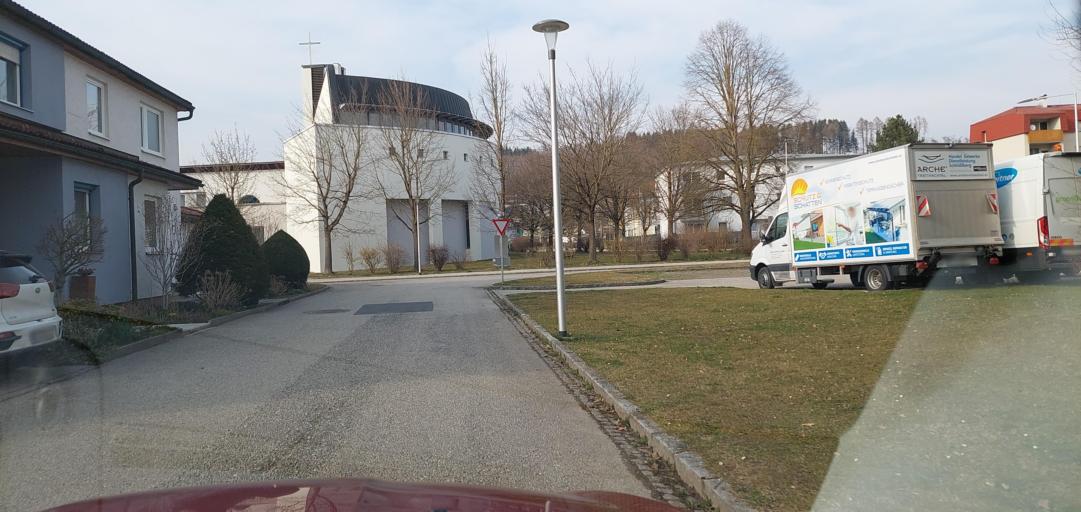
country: AT
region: Upper Austria
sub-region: Politischer Bezirk Grieskirchen
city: Grieskirchen
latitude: 48.2215
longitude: 13.8675
